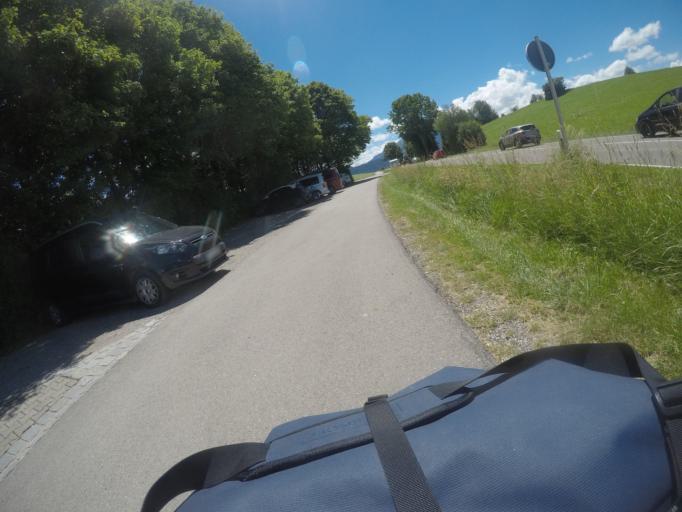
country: DE
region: Bavaria
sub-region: Swabia
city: Fuessen
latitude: 47.6075
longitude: 10.7102
